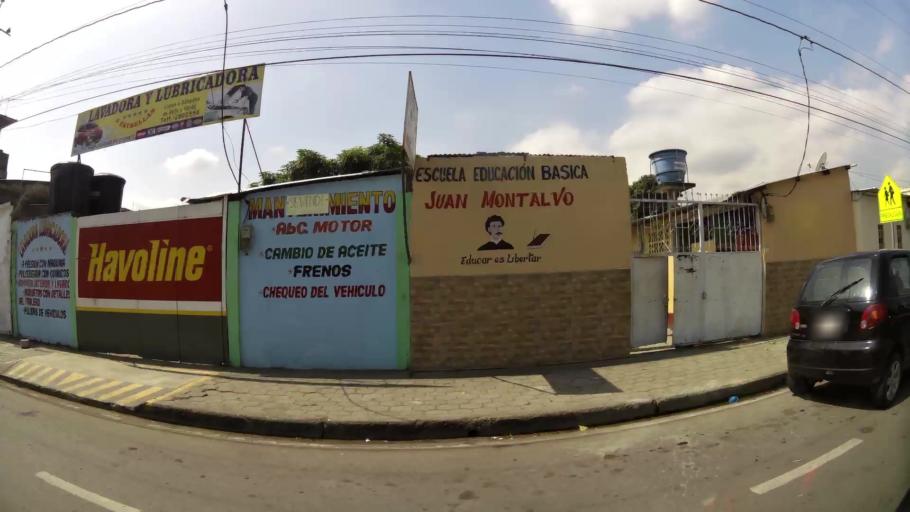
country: EC
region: Guayas
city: Eloy Alfaro
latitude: -2.1569
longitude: -79.8410
